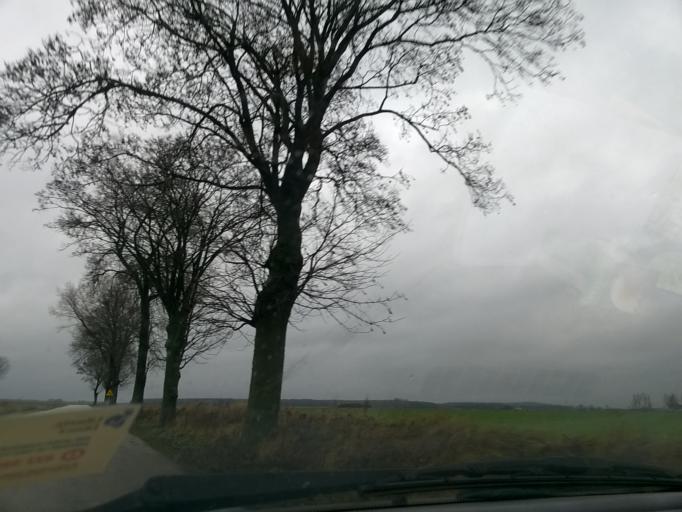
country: PL
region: Kujawsko-Pomorskie
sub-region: Powiat nakielski
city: Kcynia
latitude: 53.0103
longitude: 17.4324
